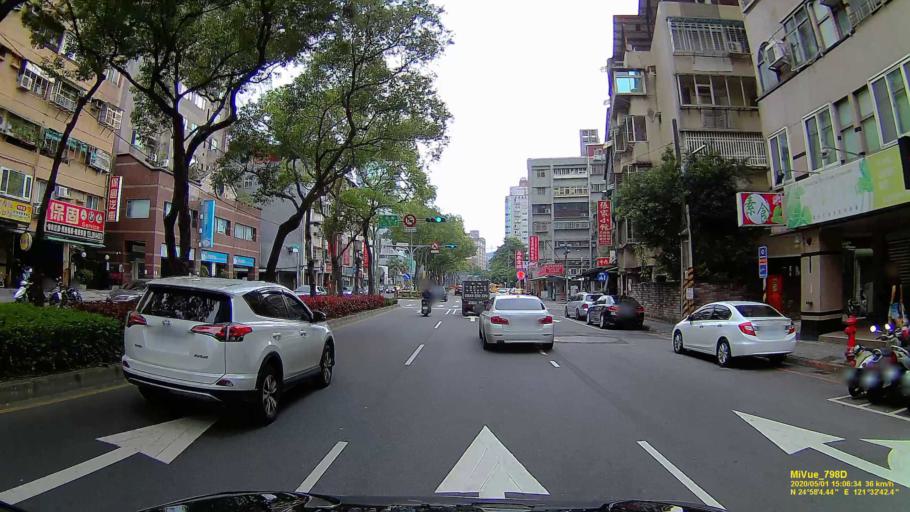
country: TW
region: Taipei
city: Taipei
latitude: 24.9678
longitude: 121.5450
